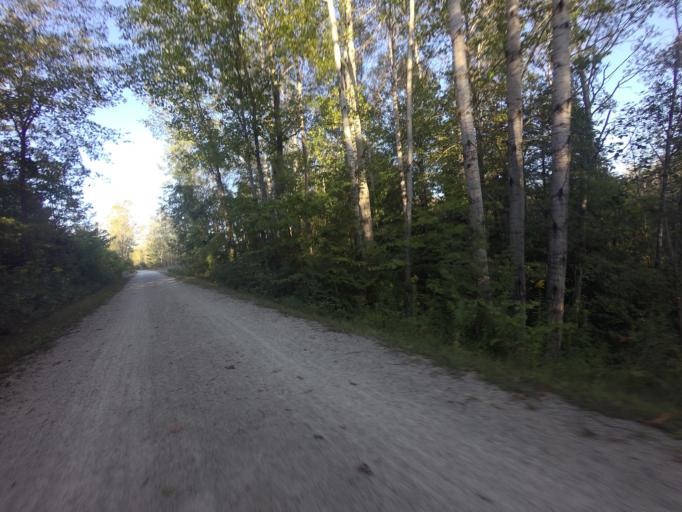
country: CA
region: Ontario
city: Brampton
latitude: 43.8334
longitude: -79.8972
